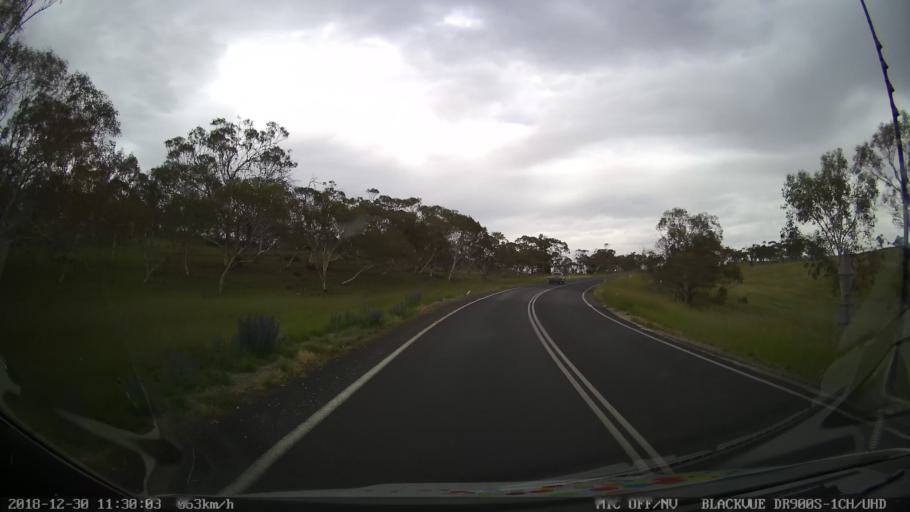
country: AU
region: New South Wales
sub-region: Snowy River
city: Jindabyne
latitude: -36.4459
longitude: 148.6070
